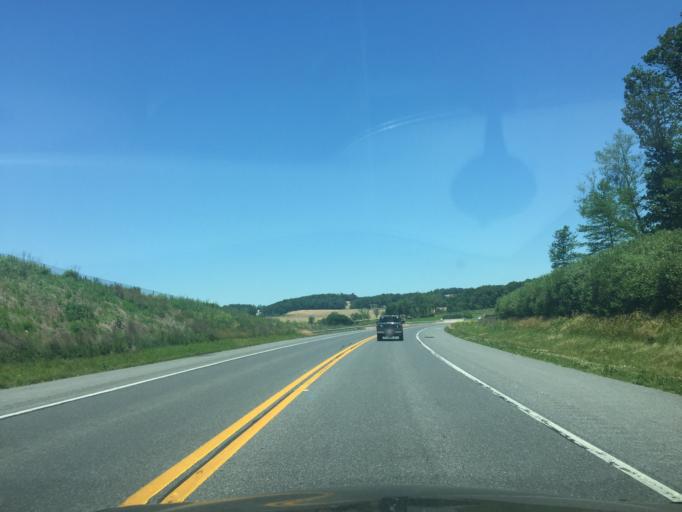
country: US
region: Maryland
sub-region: Carroll County
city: Hampstead
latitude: 39.6244
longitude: -76.8672
